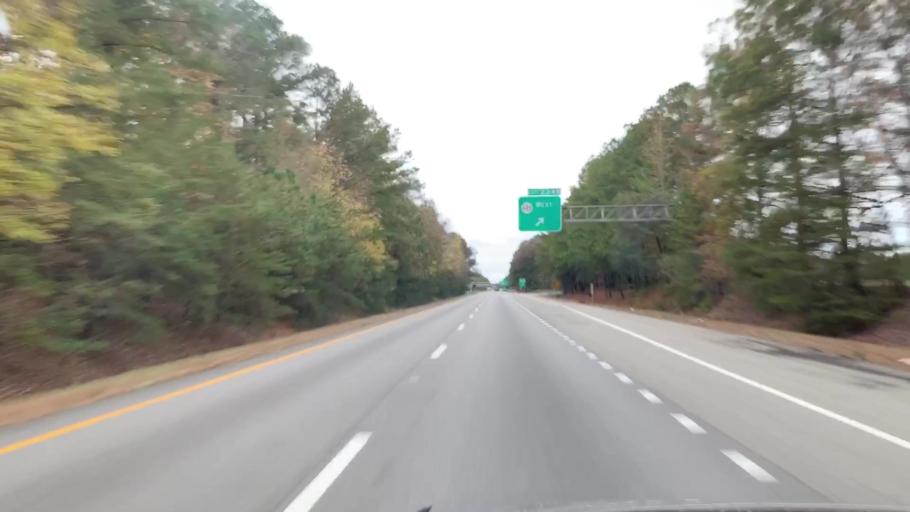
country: US
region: Virginia
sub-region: James City County
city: Williamsburg
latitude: 37.3482
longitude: -76.7261
